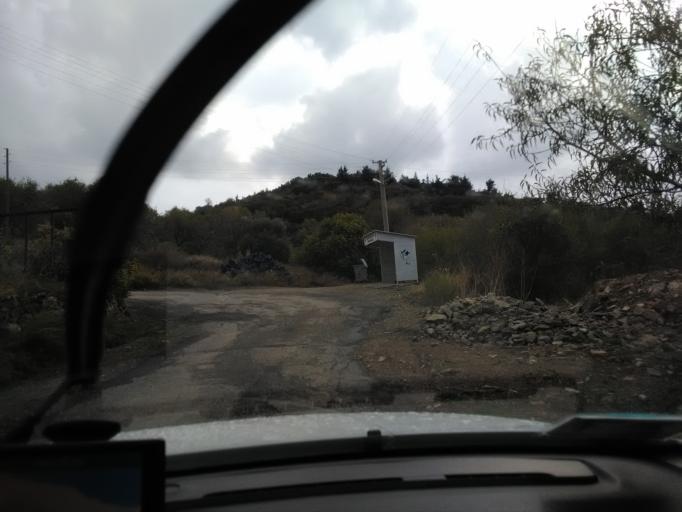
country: TR
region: Antalya
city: Gazipasa
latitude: 36.1555
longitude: 32.4253
